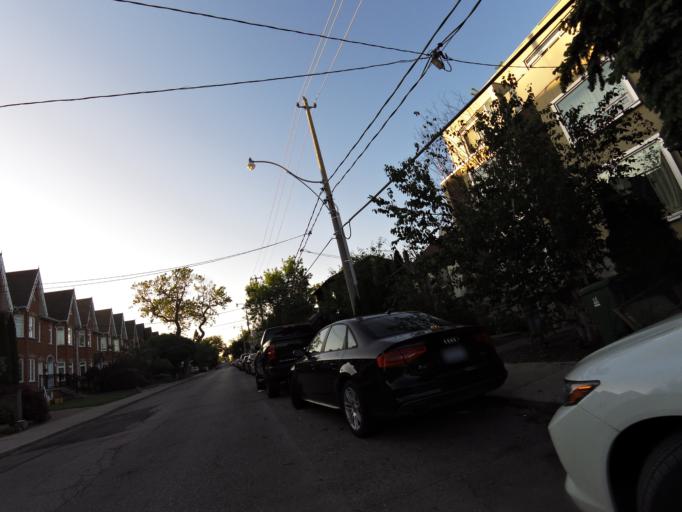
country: CA
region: Ontario
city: Toronto
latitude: 43.6488
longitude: -79.4107
